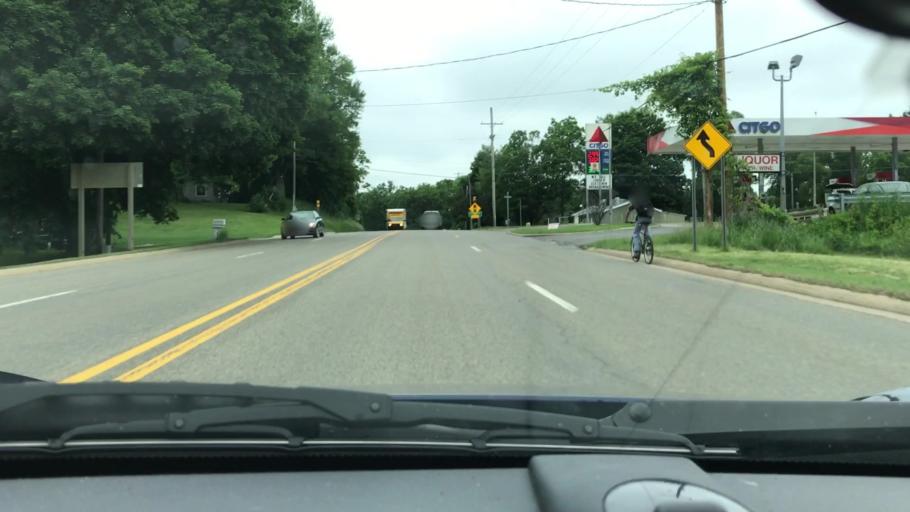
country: US
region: Michigan
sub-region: Calhoun County
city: Springfield
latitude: 42.3585
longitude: -85.2325
